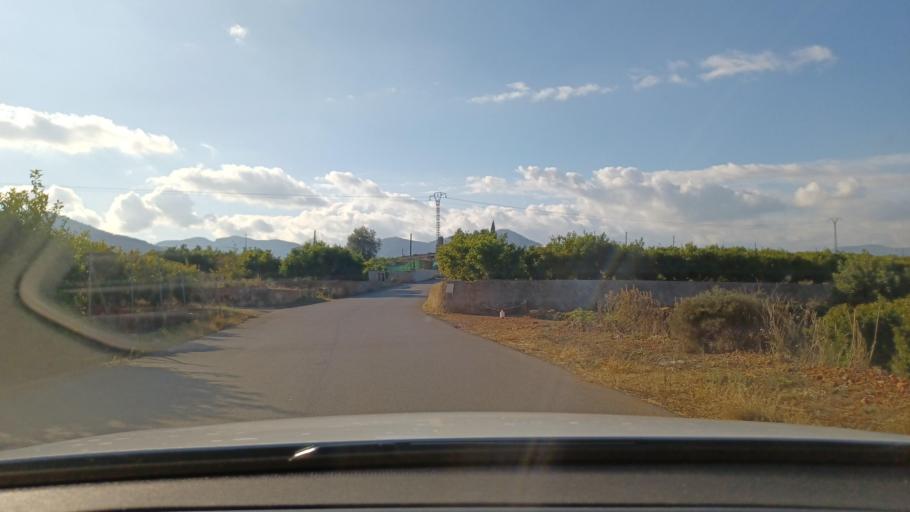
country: ES
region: Valencia
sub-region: Provincia de Castello
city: Onda
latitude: 39.9529
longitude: -0.2337
